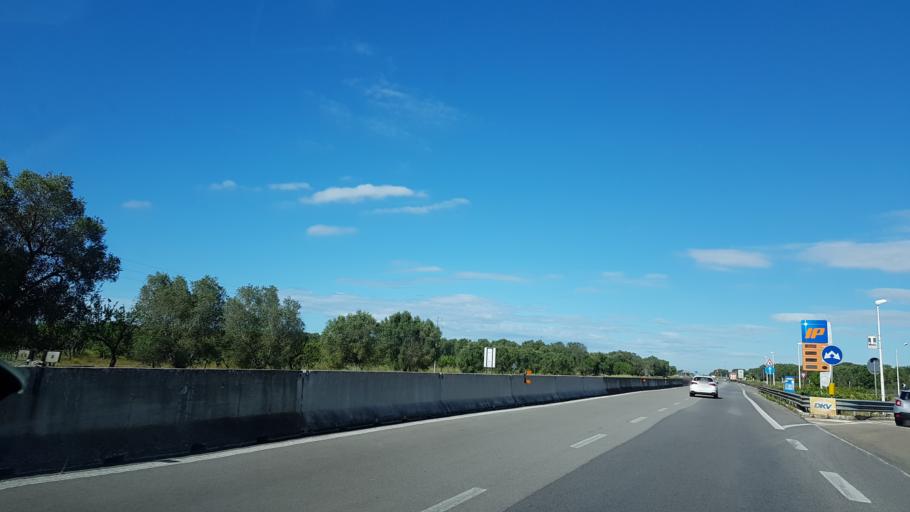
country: IT
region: Apulia
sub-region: Provincia di Brindisi
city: Latiano
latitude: 40.5451
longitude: 17.6886
